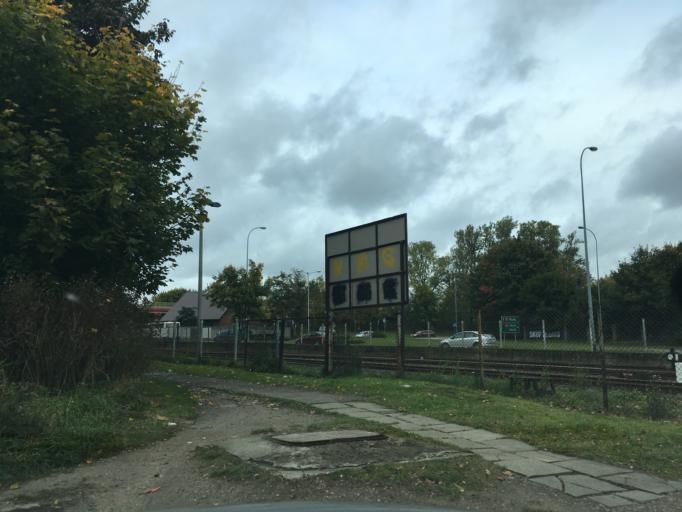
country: PL
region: Pomeranian Voivodeship
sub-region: Powiat koscierski
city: Koscierzyna
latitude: 54.1233
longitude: 17.9912
